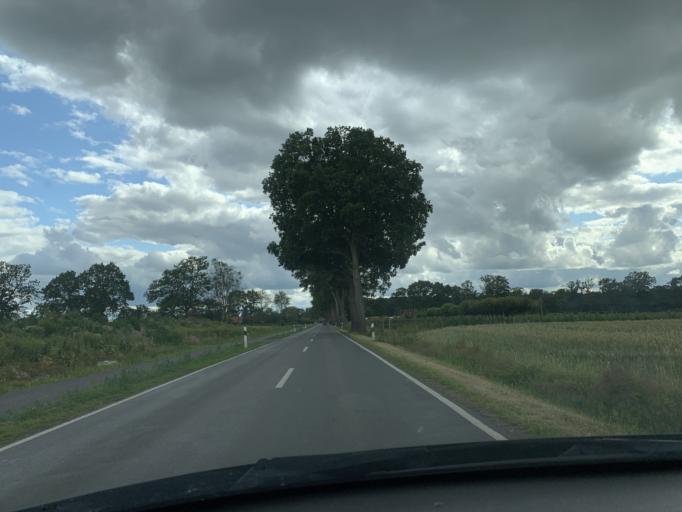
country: DE
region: Lower Saxony
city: Westerstede
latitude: 53.2182
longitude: 7.9400
